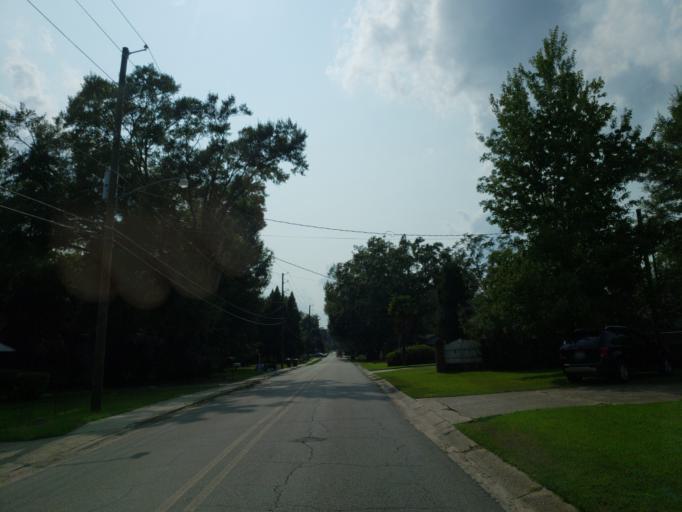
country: US
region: Mississippi
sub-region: Lamar County
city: West Hattiesburg
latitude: 31.3212
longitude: -89.3382
